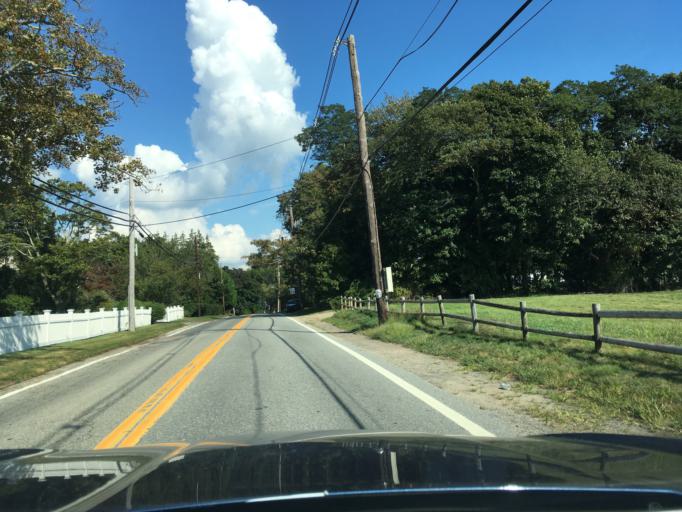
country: US
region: Rhode Island
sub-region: Bristol County
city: Barrington
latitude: 41.7286
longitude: -71.3245
